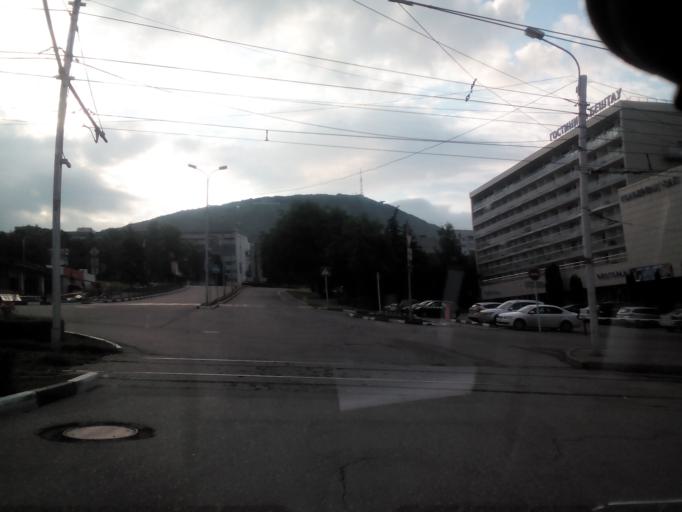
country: RU
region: Stavropol'skiy
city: Pyatigorsk
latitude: 44.0531
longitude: 43.0630
